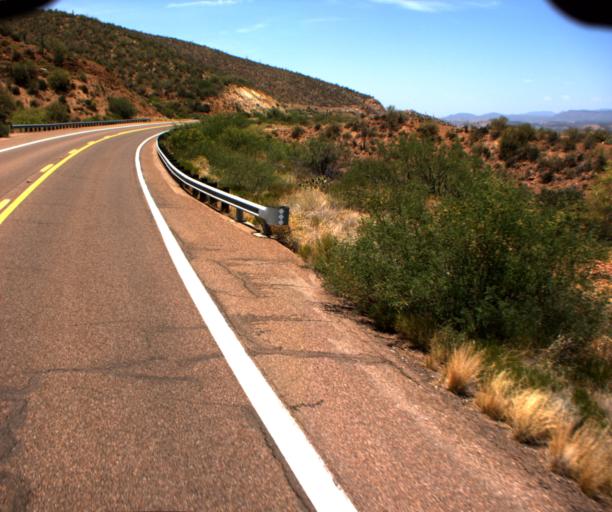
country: US
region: Arizona
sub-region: Gila County
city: Tonto Basin
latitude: 33.6840
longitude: -111.1711
